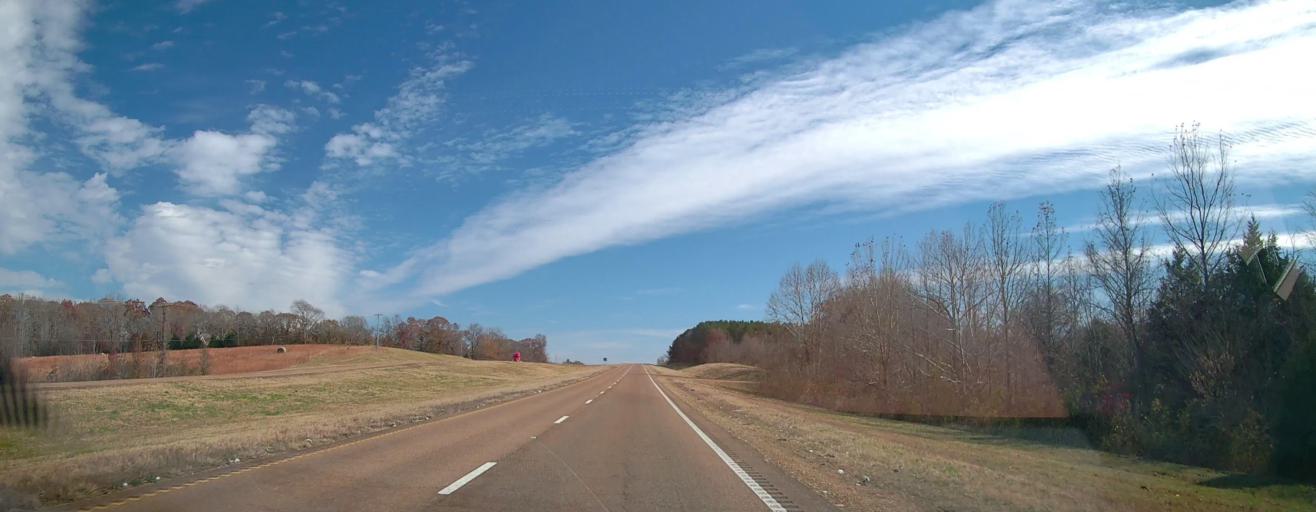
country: US
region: Mississippi
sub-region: Marshall County
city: Holly Springs
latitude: 34.9461
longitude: -89.3740
